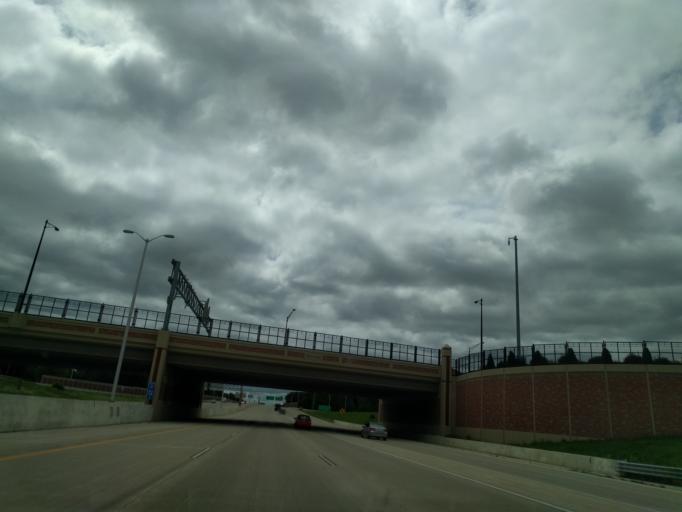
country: US
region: Wisconsin
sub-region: Brown County
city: Howard
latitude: 44.5248
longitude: -88.0821
